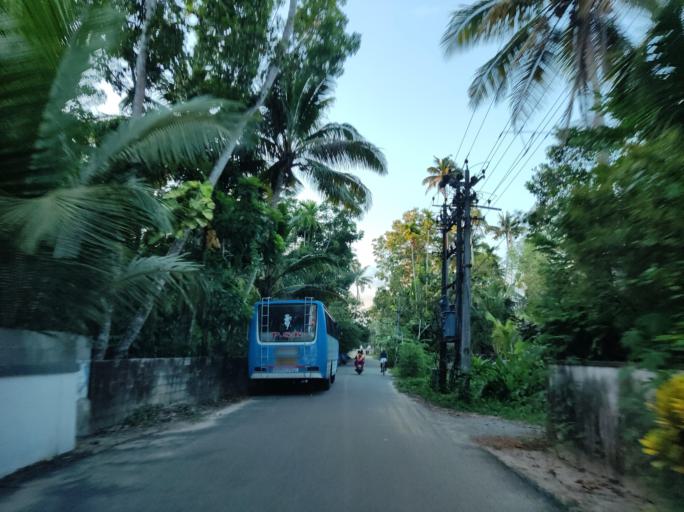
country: IN
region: Kerala
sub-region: Alappuzha
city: Vayalar
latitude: 9.7173
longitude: 76.2969
